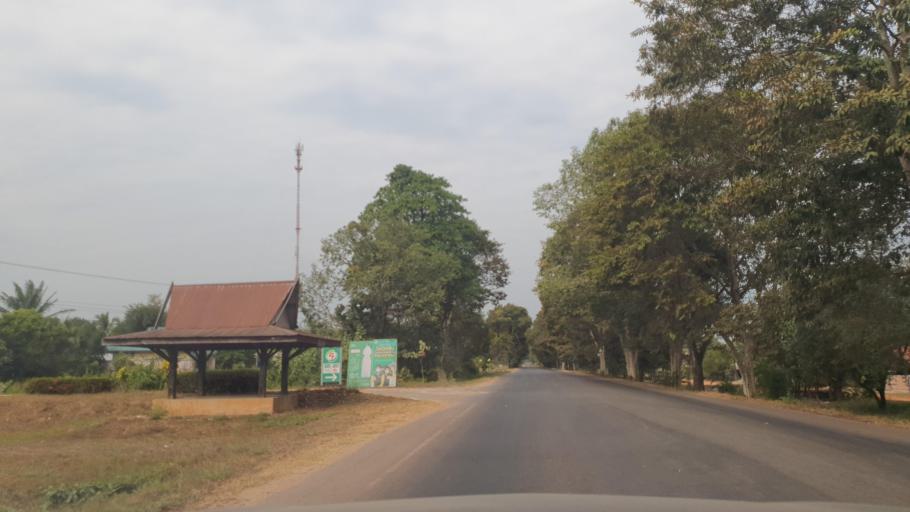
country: TH
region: Changwat Bueng Kan
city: Bung Khla
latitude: 18.2263
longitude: 104.0335
